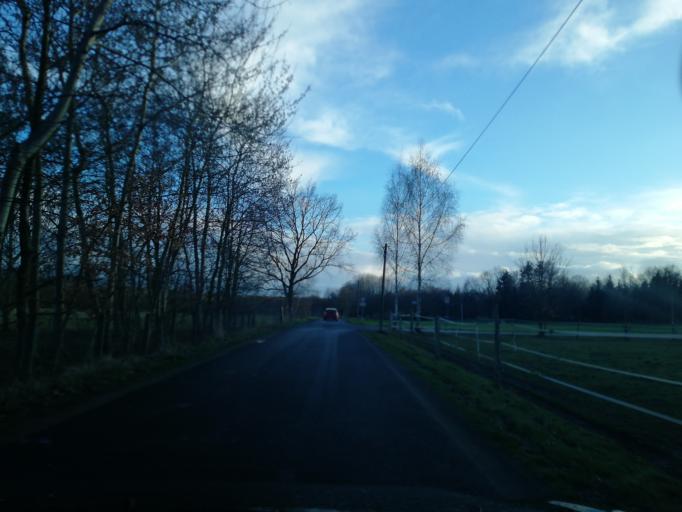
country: DE
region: Brandenburg
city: Calau
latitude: 51.7353
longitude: 13.9606
